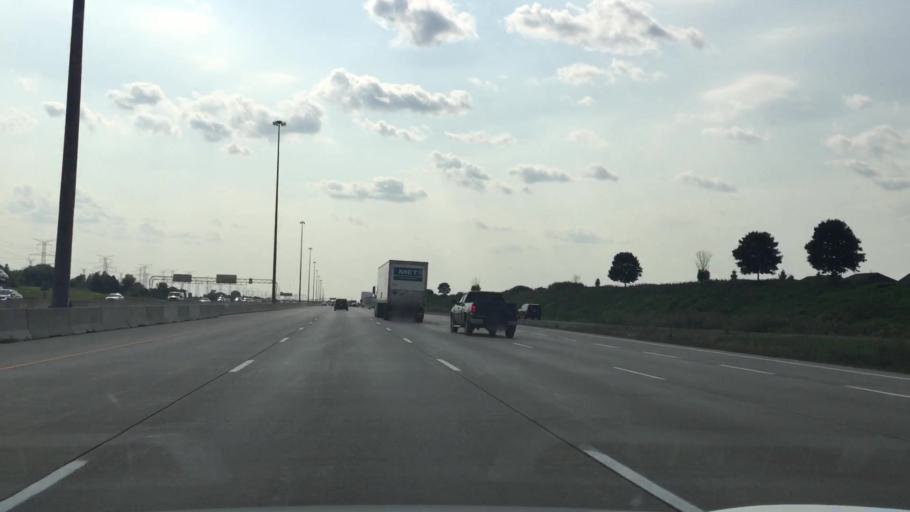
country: CA
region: Ontario
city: Markham
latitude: 43.8562
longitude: -79.2839
